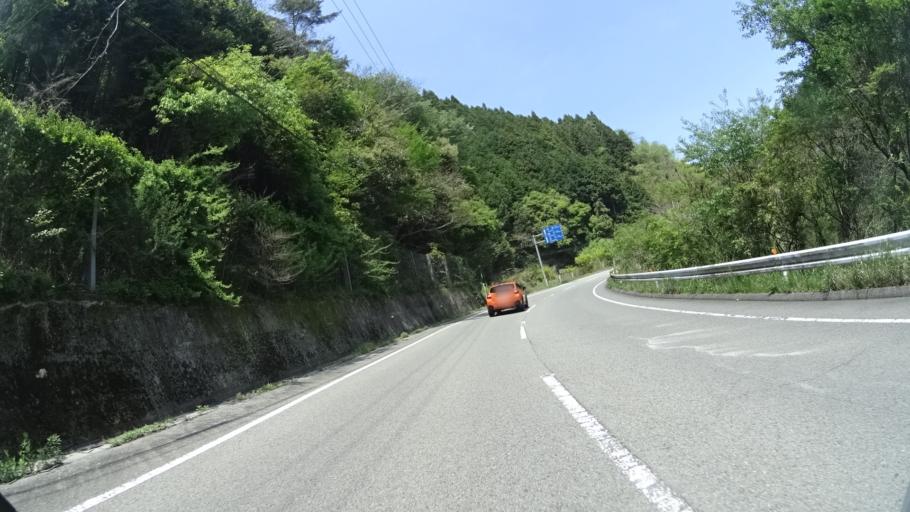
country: JP
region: Ehime
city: Hojo
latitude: 33.9226
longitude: 132.8863
